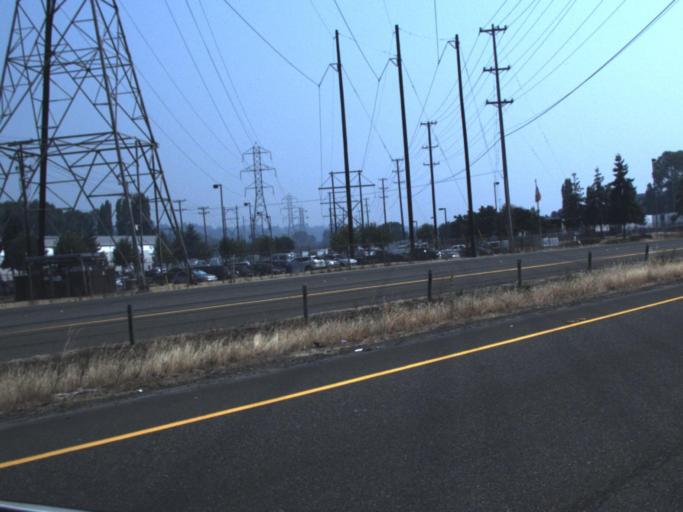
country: US
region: Washington
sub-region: King County
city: Boulevard Park
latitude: 47.5064
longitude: -122.3003
